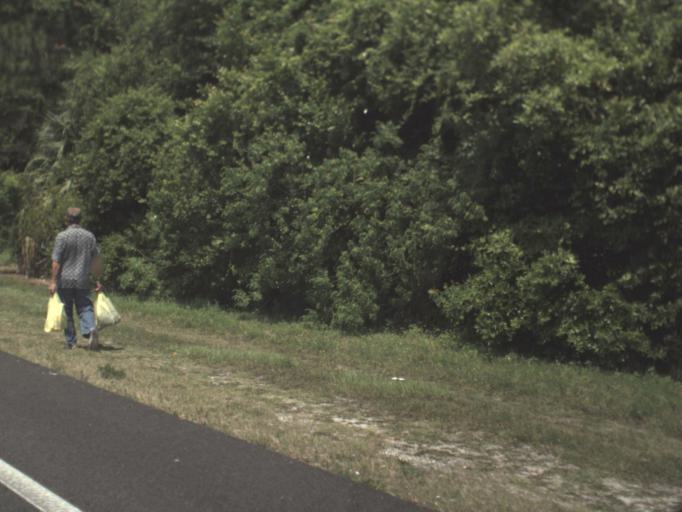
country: US
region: Florida
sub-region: Clay County
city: Bellair-Meadowbrook Terrace
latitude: 30.2851
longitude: -81.8057
